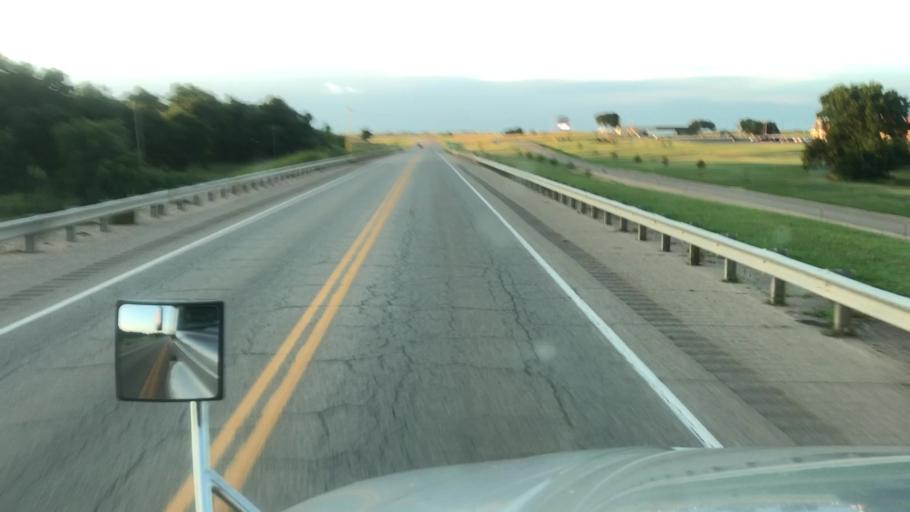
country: US
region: Oklahoma
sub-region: Osage County
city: McCord
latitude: 36.4958
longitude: -97.0737
